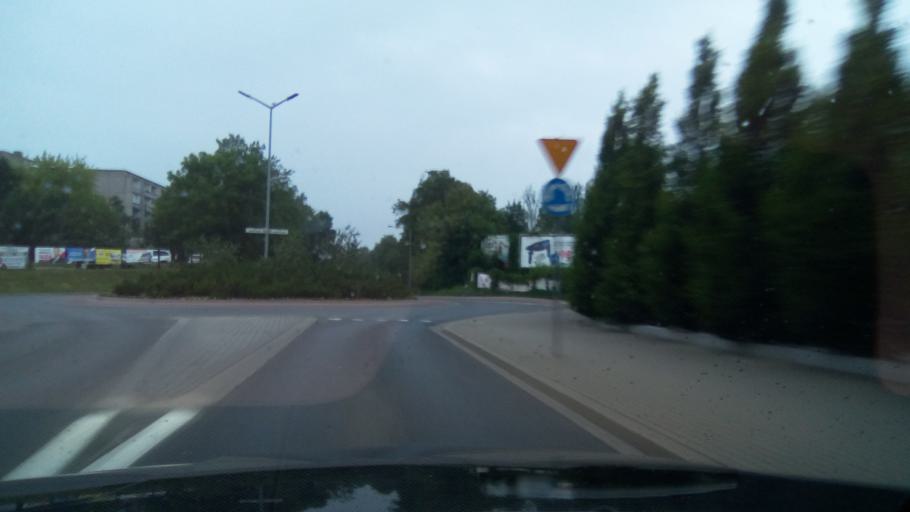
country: PL
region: Greater Poland Voivodeship
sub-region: Powiat poznanski
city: Swarzedz
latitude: 52.4212
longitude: 17.0832
